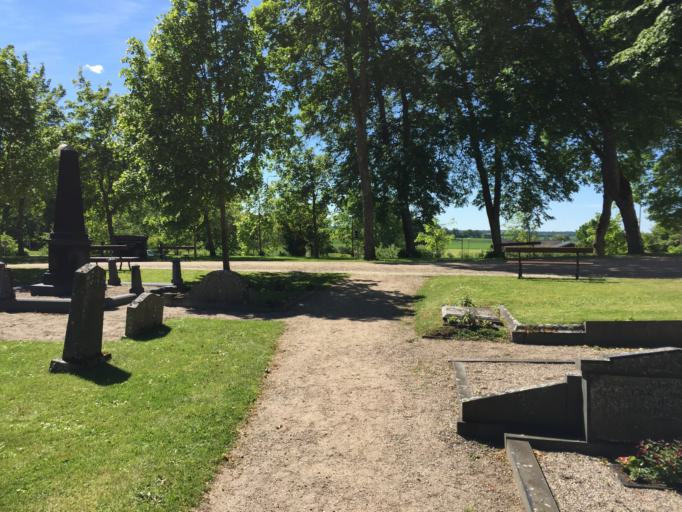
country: SE
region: Soedermanland
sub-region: Vingakers Kommun
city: Vingaker
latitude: 59.0528
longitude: 15.8789
